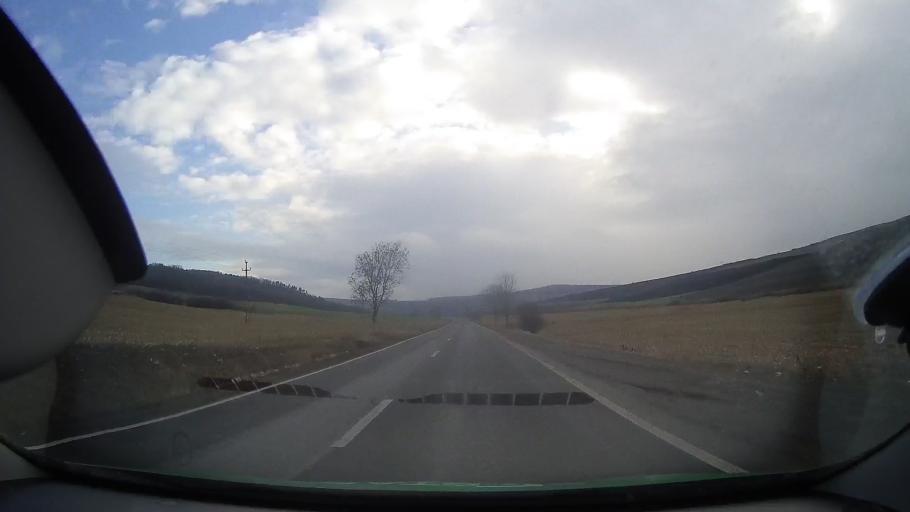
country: RO
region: Mures
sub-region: Comuna Cucerdea
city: Cucerdea
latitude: 46.3755
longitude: 24.2576
